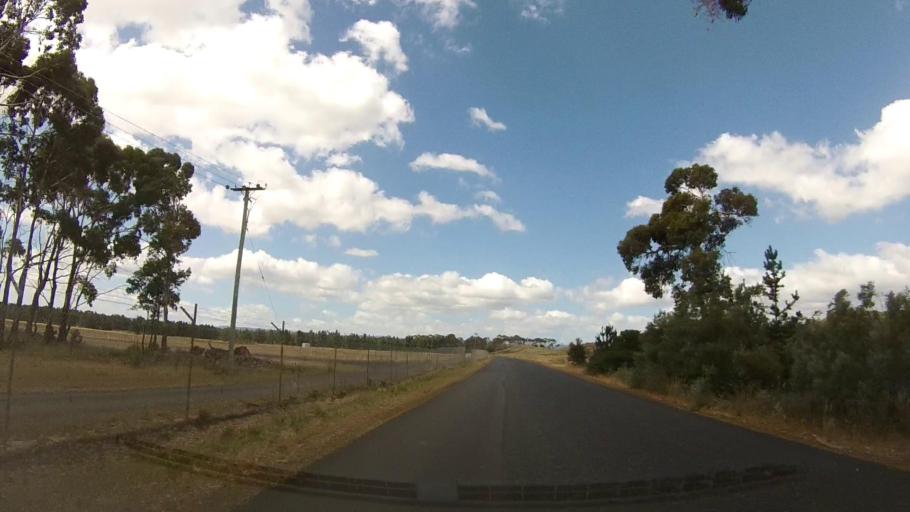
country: AU
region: Tasmania
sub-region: Clarence
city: Seven Mile Beach
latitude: -42.8480
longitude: 147.5233
